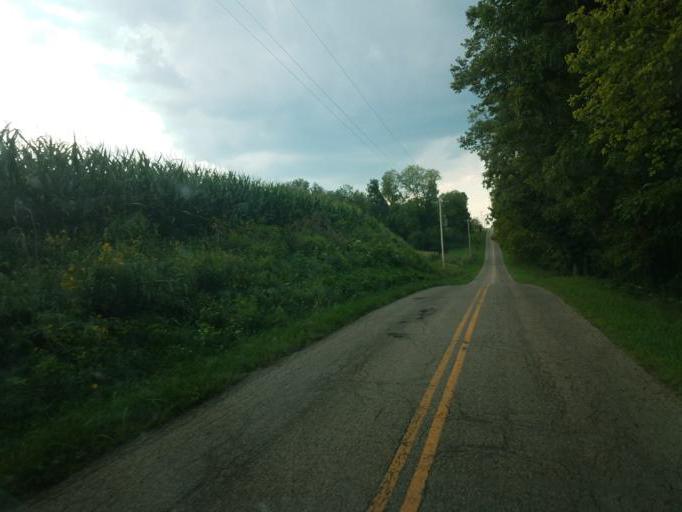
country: US
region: Ohio
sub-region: Knox County
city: Gambier
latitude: 40.3750
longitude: -82.3479
